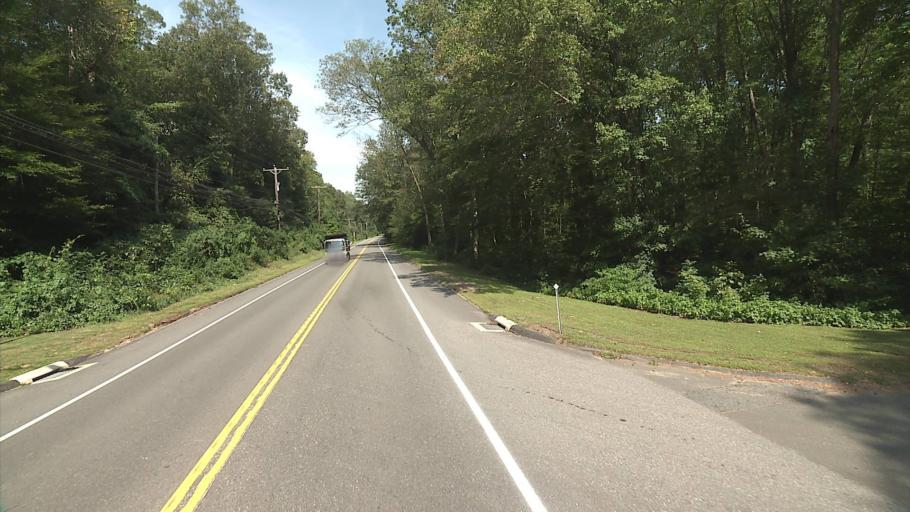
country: US
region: Connecticut
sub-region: New Haven County
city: Madison Center
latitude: 41.3398
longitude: -72.6287
